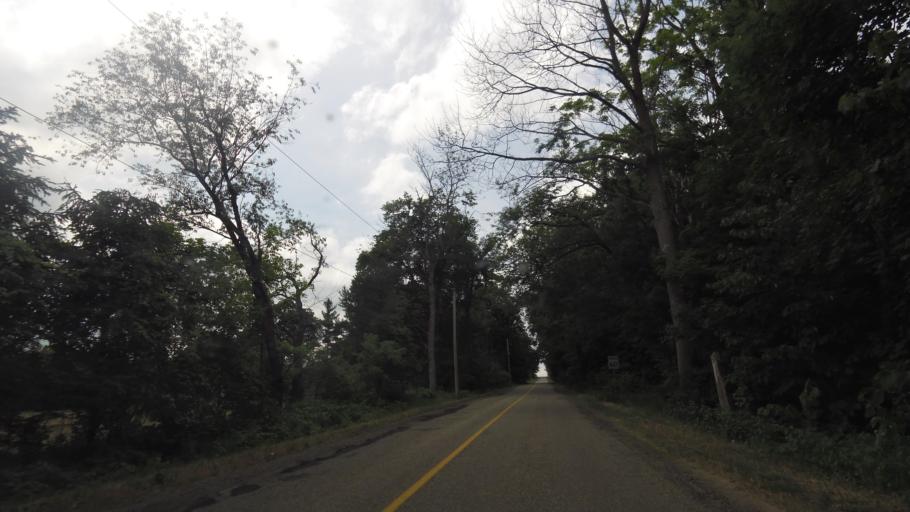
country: CA
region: Ontario
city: Brampton
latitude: 43.8554
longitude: -79.8936
